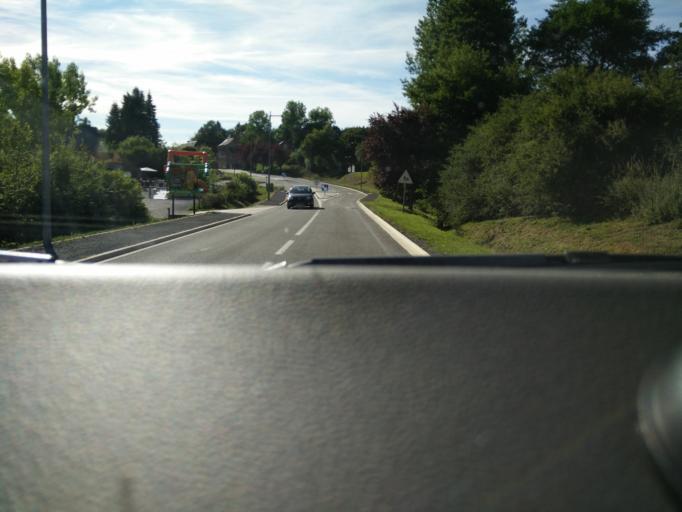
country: FR
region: Nord-Pas-de-Calais
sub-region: Departement du Nord
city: Trelon
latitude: 50.1210
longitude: 4.1009
